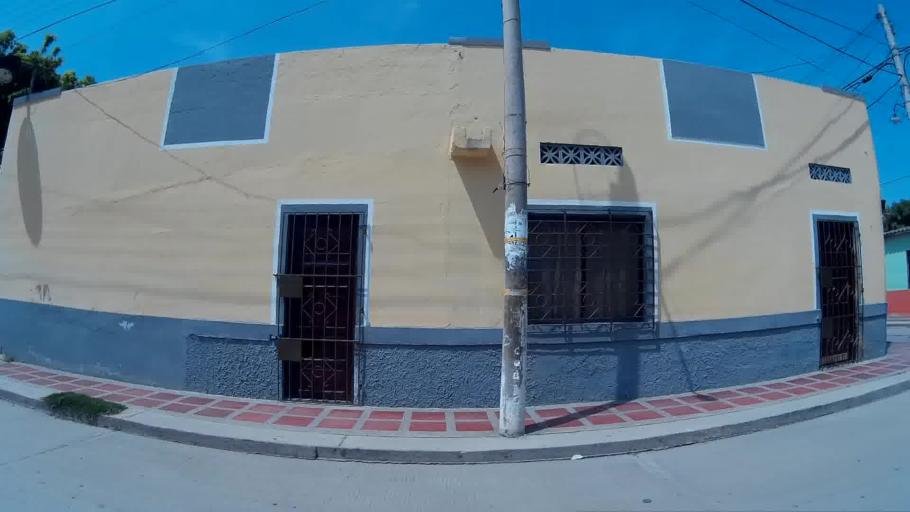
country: CO
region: Magdalena
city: Cienaga
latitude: 11.0143
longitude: -74.2471
